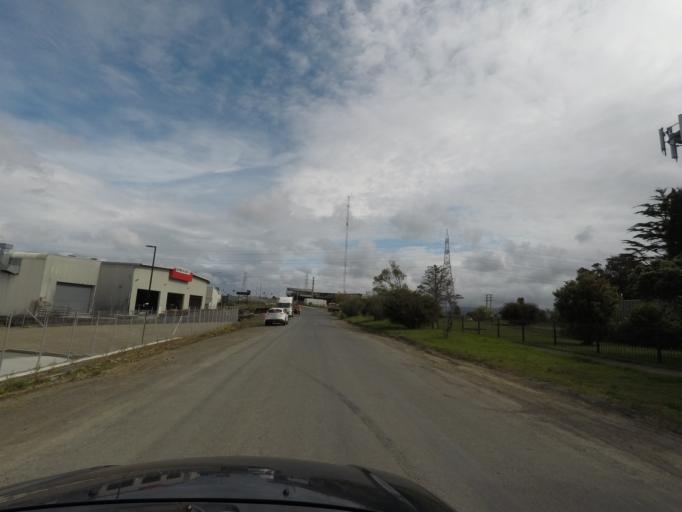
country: NZ
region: Auckland
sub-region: Auckland
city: Rosebank
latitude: -36.8454
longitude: 174.6317
